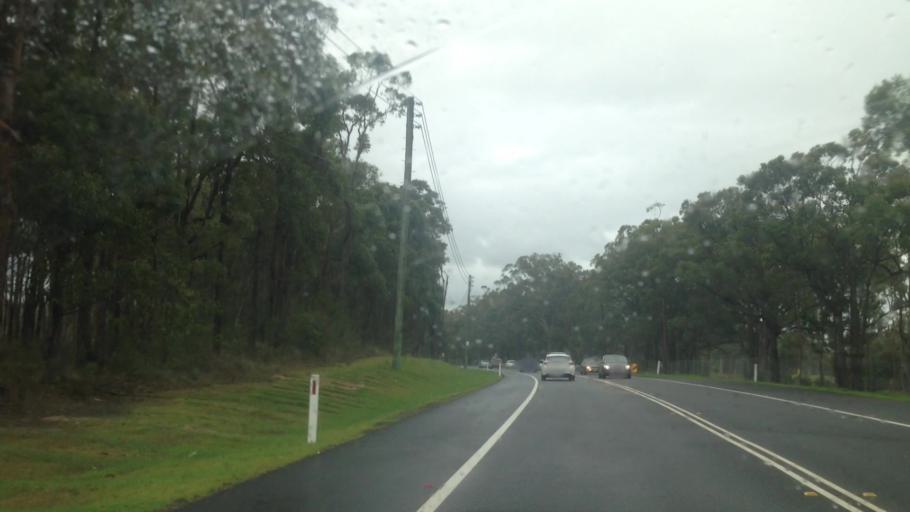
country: AU
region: New South Wales
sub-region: Lake Macquarie Shire
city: Dora Creek
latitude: -33.1209
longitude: 151.4771
